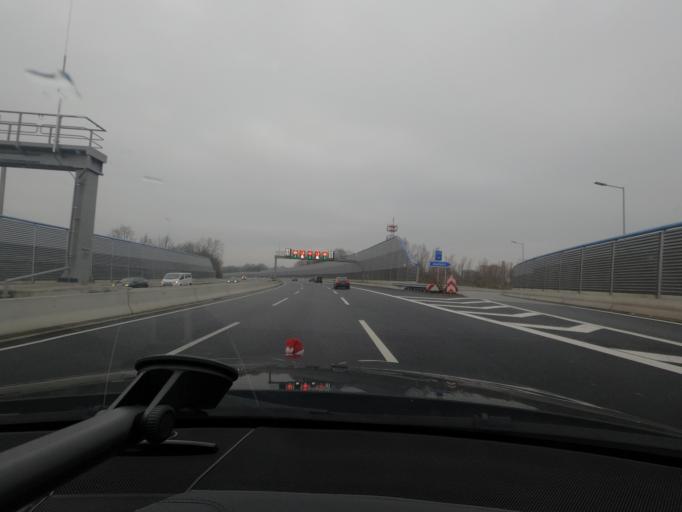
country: DE
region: Hamburg
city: Eidelstedt
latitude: 53.6185
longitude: 9.9132
